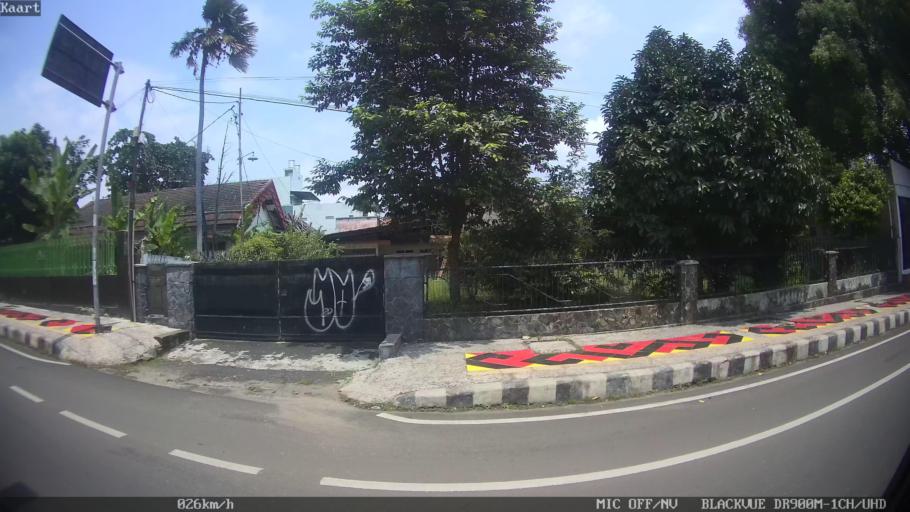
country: ID
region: Lampung
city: Bandarlampung
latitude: -5.4234
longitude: 105.2693
